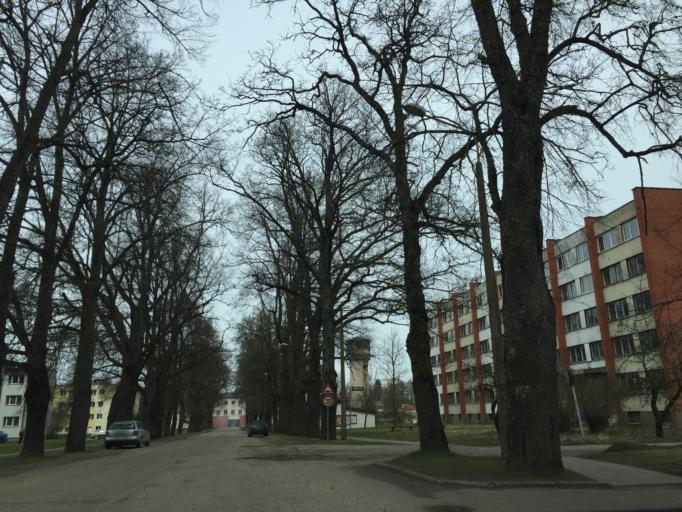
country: LV
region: Priekuli
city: Priekuli
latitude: 57.3522
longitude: 25.3319
